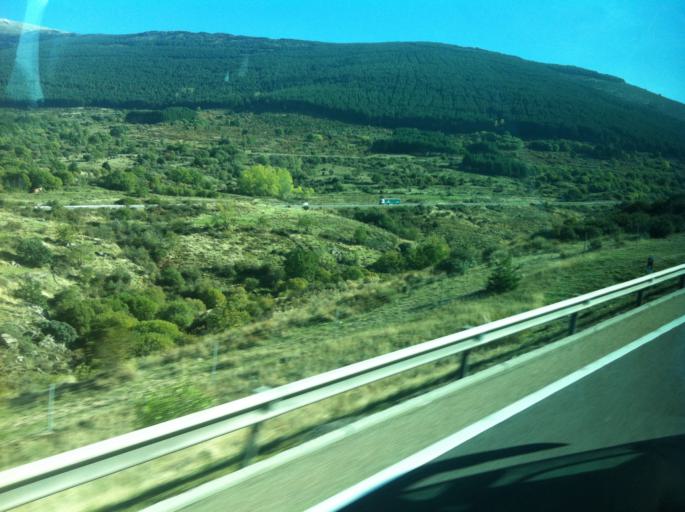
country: ES
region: Madrid
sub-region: Provincia de Madrid
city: Somosierra
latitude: 41.1741
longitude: -3.5827
